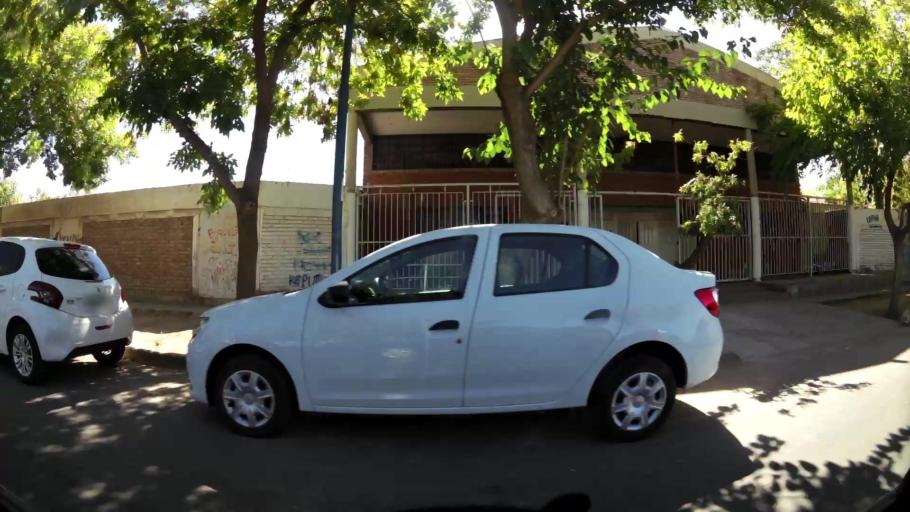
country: AR
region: Mendoza
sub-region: Departamento de Godoy Cruz
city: Godoy Cruz
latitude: -32.9535
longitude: -68.8228
